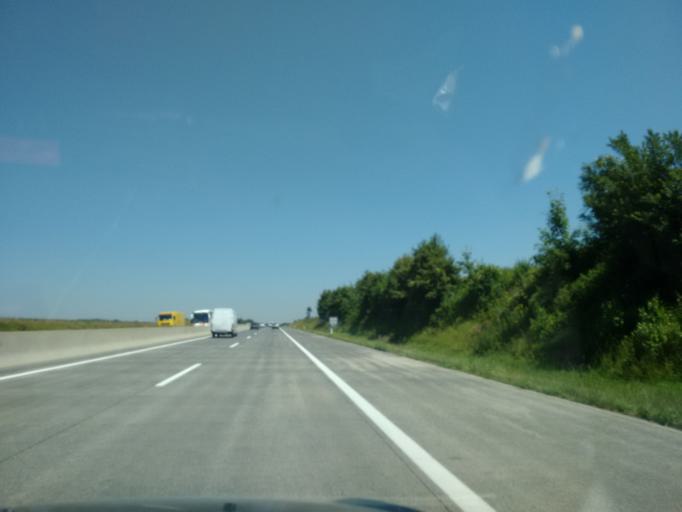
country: AT
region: Upper Austria
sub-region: Politischer Bezirk Gmunden
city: Vorchdorf
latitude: 48.0184
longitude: 13.9490
